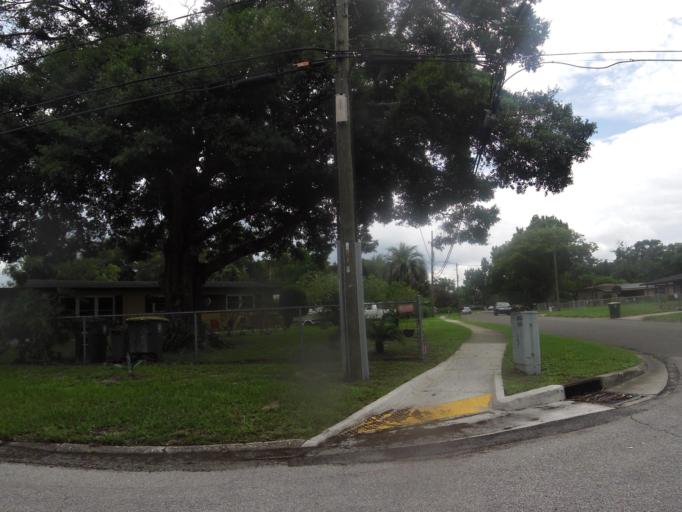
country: US
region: Florida
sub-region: Duval County
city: Jacksonville
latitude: 30.3149
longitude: -81.5371
